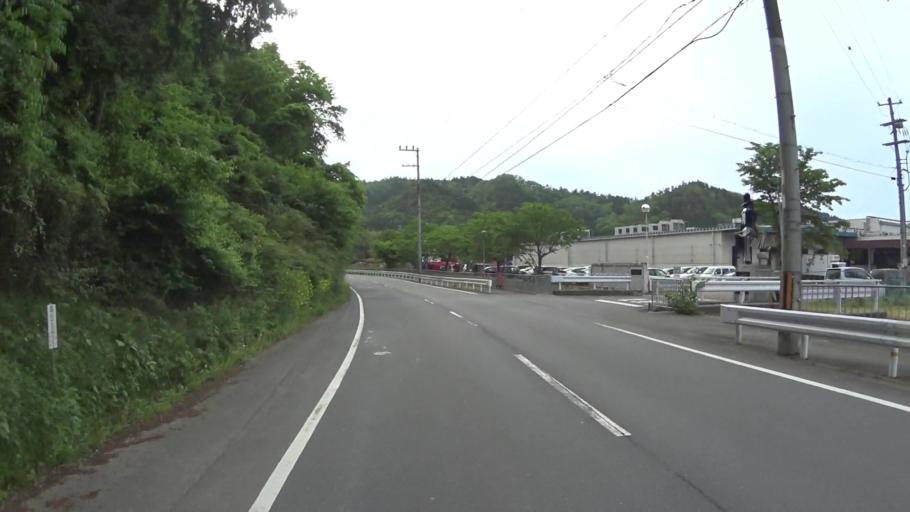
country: JP
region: Kyoto
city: Kameoka
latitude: 35.1047
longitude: 135.5203
